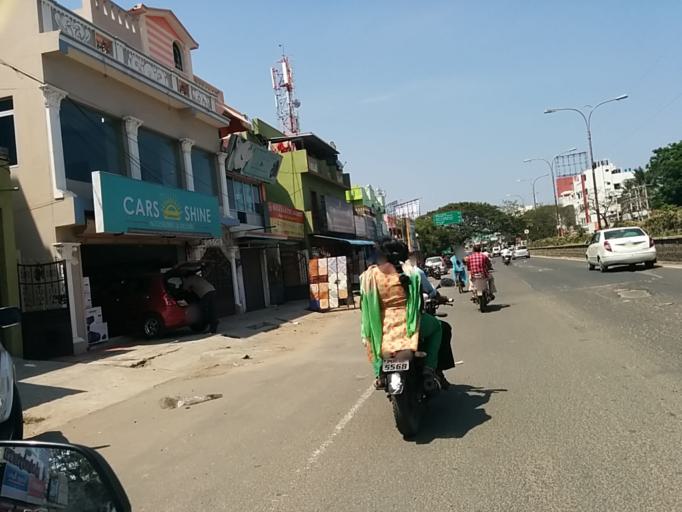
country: IN
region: Pondicherry
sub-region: Puducherry
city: Puducherry
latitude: 11.9294
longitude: 79.8075
